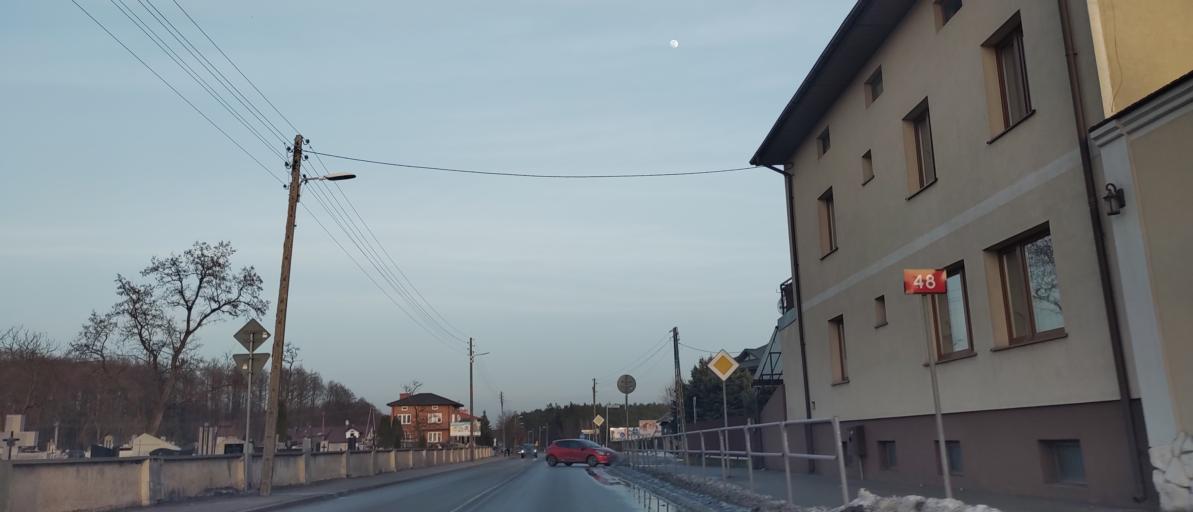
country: PL
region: Masovian Voivodeship
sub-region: Powiat bialobrzeski
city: Bialobrzegi
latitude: 51.6466
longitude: 20.9572
